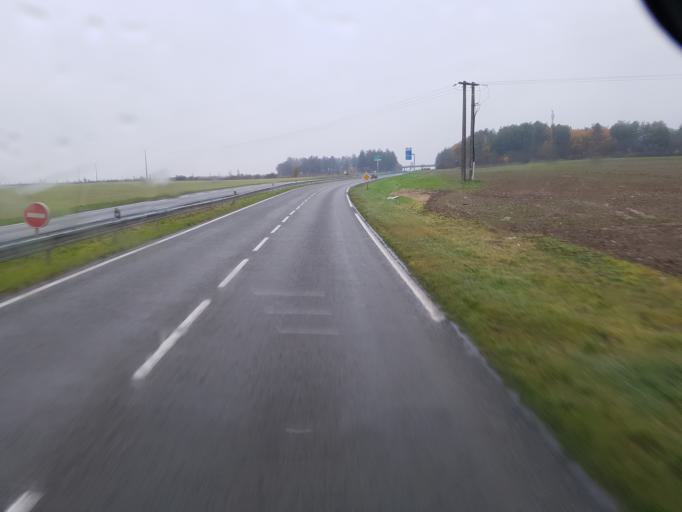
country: FR
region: Picardie
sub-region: Departement de l'Aisne
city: Gauchy
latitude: 49.8101
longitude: 3.2871
